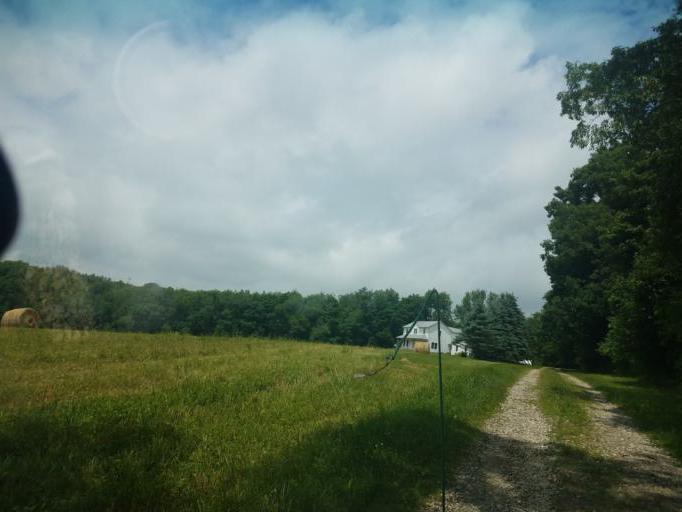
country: US
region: Ohio
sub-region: Sandusky County
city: Bellville
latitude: 40.5580
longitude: -82.4945
